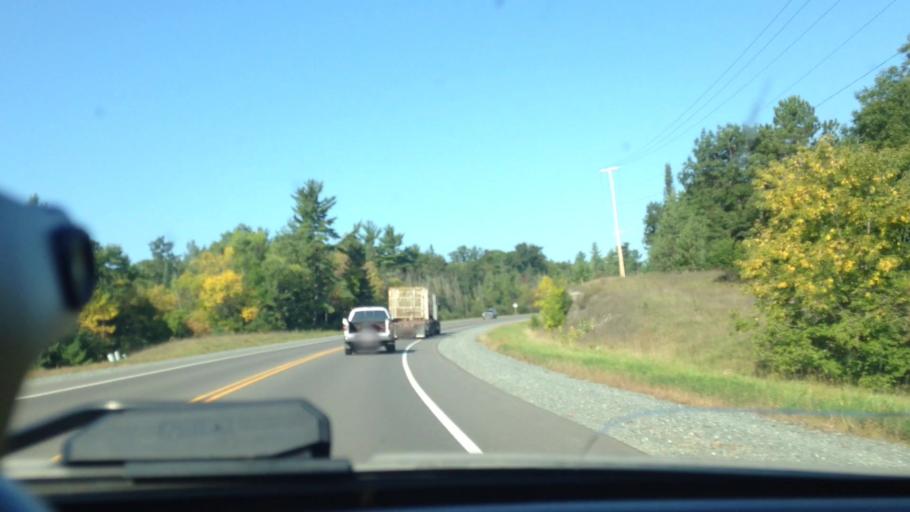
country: US
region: Michigan
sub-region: Dickinson County
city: Iron Mountain
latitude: 45.8662
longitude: -88.0767
